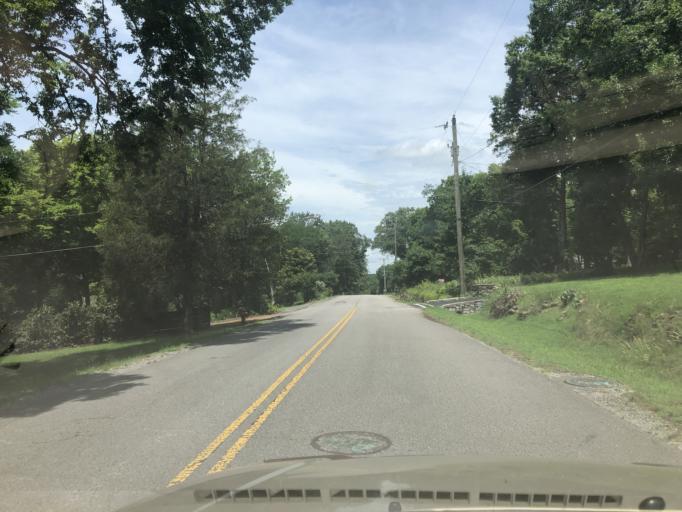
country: US
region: Tennessee
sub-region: Davidson County
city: Lakewood
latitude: 36.2452
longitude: -86.6850
